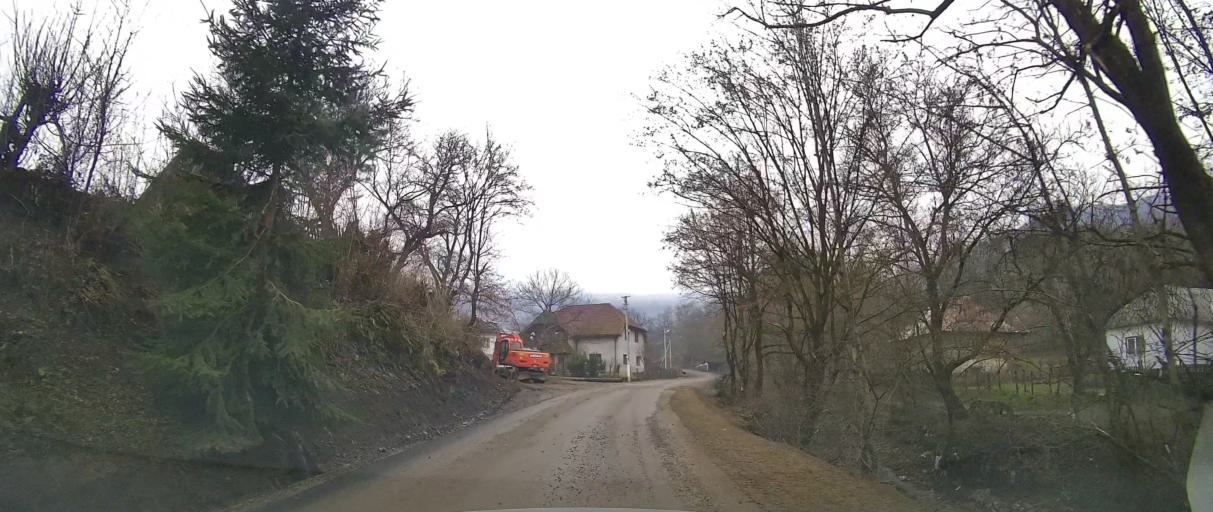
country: UA
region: Zakarpattia
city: Velykyi Bereznyi
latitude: 48.9674
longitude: 22.5510
